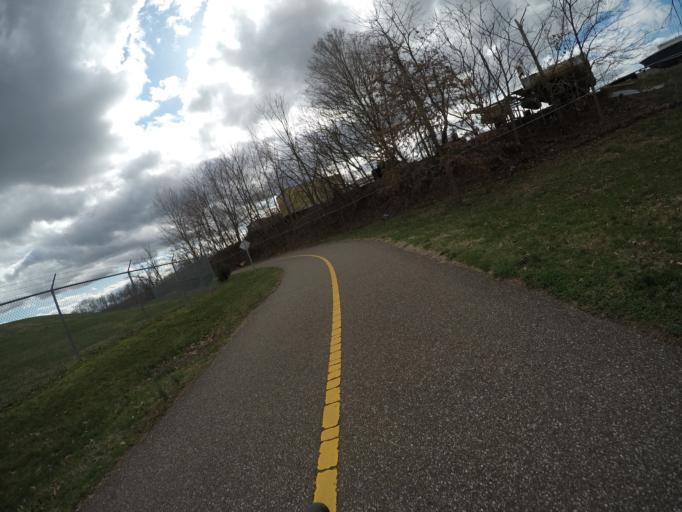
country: US
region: West Virginia
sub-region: Wood County
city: Williamstown
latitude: 39.4102
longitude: -81.4371
